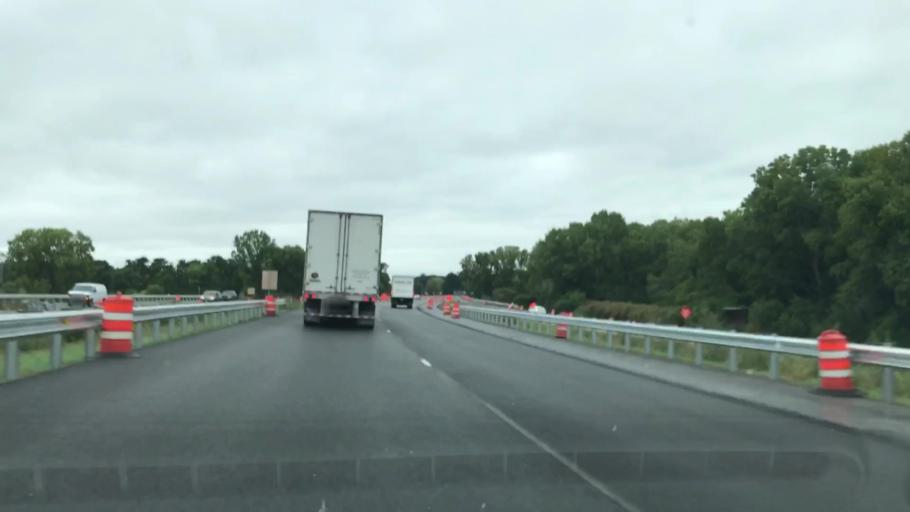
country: US
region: Wisconsin
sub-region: Brown County
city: Suamico
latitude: 44.6345
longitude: -88.0464
